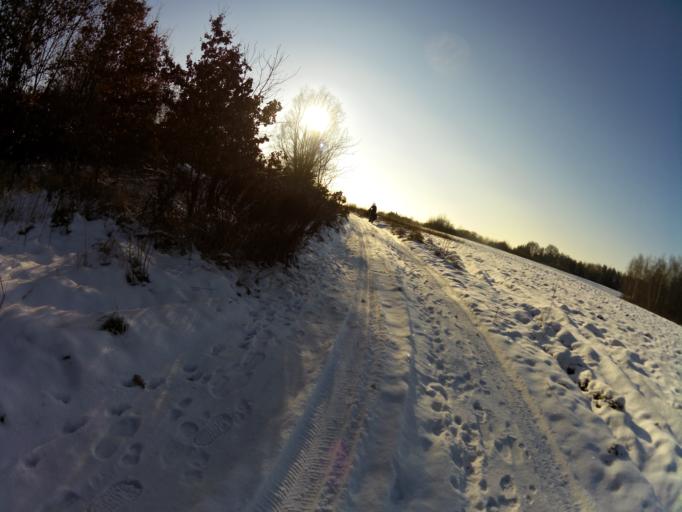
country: PL
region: West Pomeranian Voivodeship
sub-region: Powiat stargardzki
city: Dobrzany
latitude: 53.3422
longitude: 15.4143
